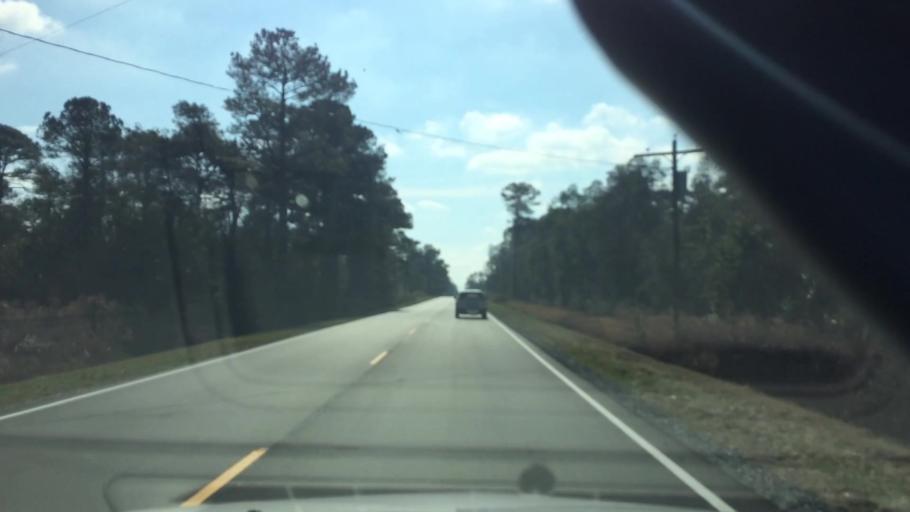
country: US
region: North Carolina
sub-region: Duplin County
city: Beulaville
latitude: 34.9860
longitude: -77.7586
